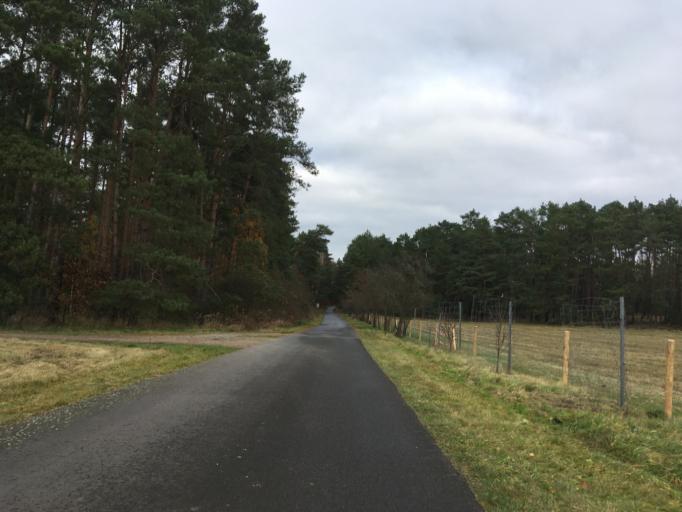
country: DE
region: Brandenburg
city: Jamlitz
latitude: 52.0308
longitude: 14.4680
